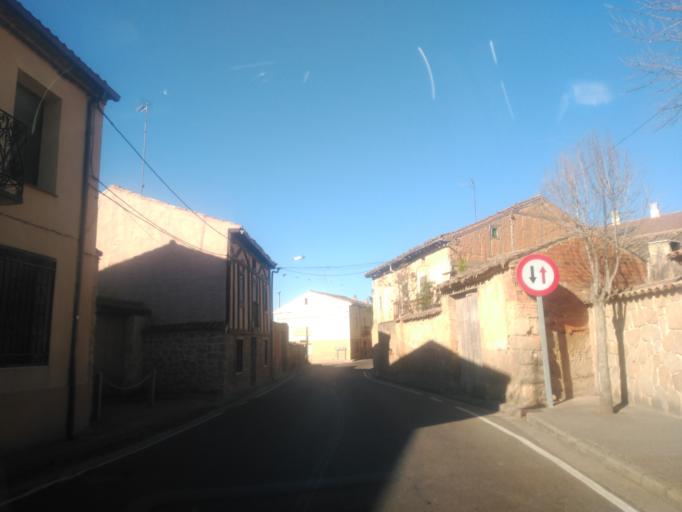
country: ES
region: Castille and Leon
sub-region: Provincia de Burgos
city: Zazuar
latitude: 41.6948
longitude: -3.5545
